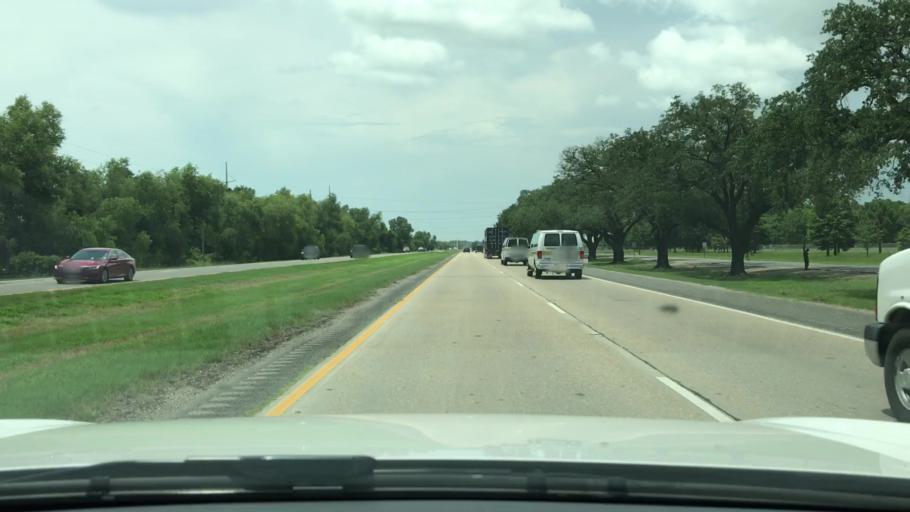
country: US
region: Louisiana
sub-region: West Baton Rouge Parish
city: Addis
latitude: 30.3265
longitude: -91.2543
